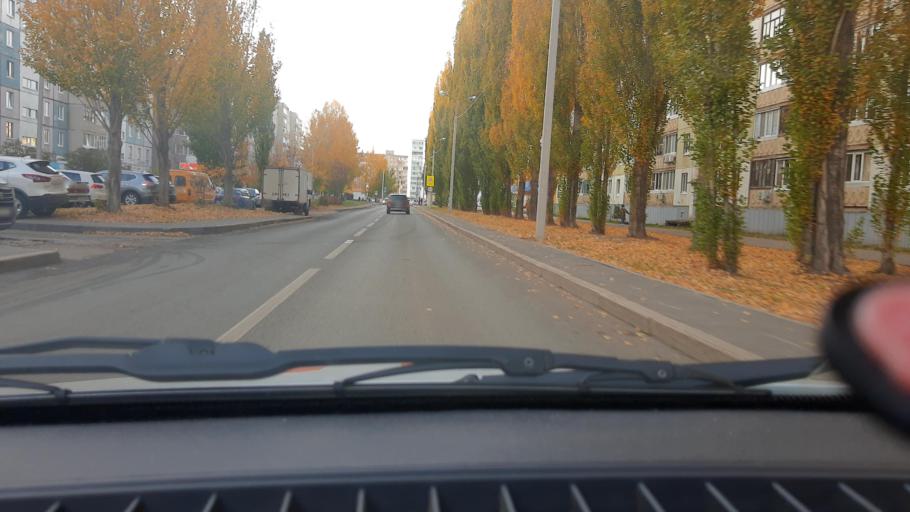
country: RU
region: Bashkortostan
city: Ufa
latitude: 54.7624
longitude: 56.0671
